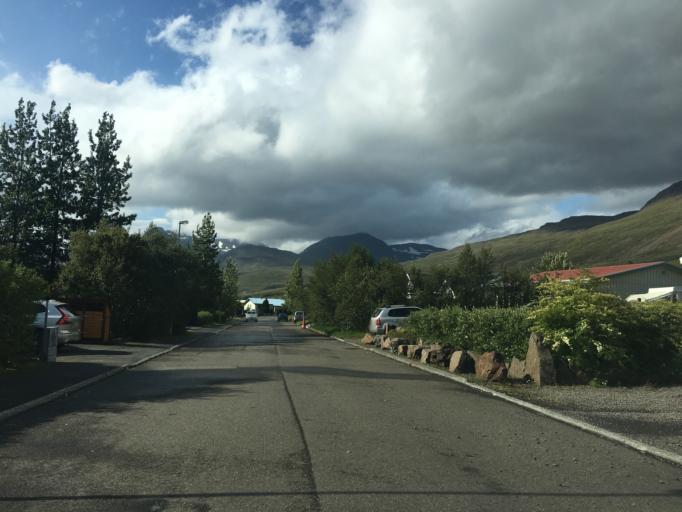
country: IS
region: East
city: Reydarfjoerdur
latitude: 65.0356
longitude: -14.2063
